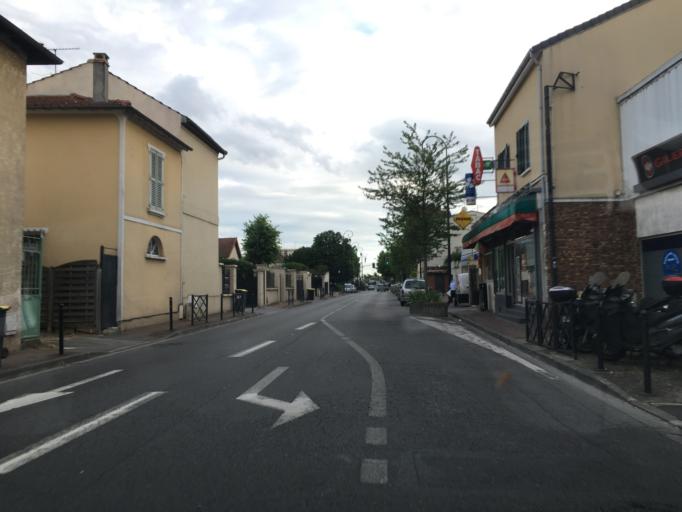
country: FR
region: Ile-de-France
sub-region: Departement du Val-de-Marne
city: Saint-Maur-des-Fosses
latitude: 48.7873
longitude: 2.4953
